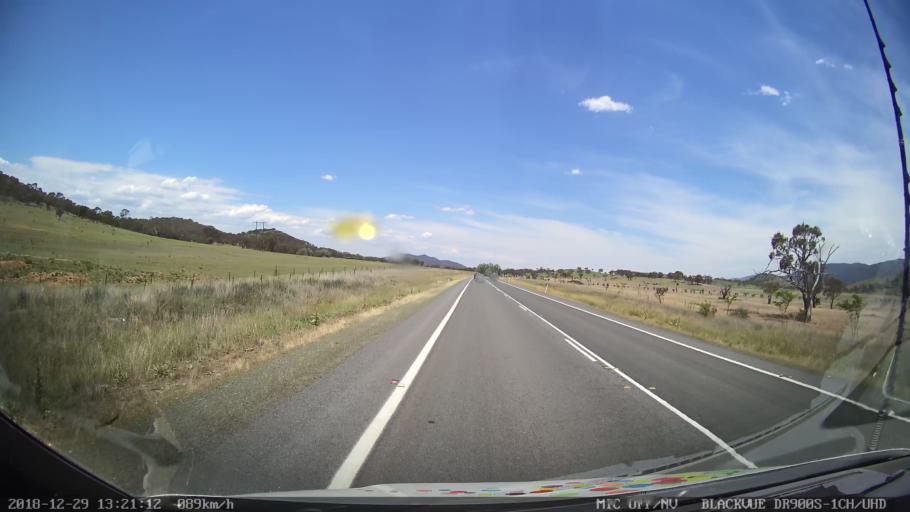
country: AU
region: Australian Capital Territory
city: Macarthur
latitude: -35.7890
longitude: 149.1635
